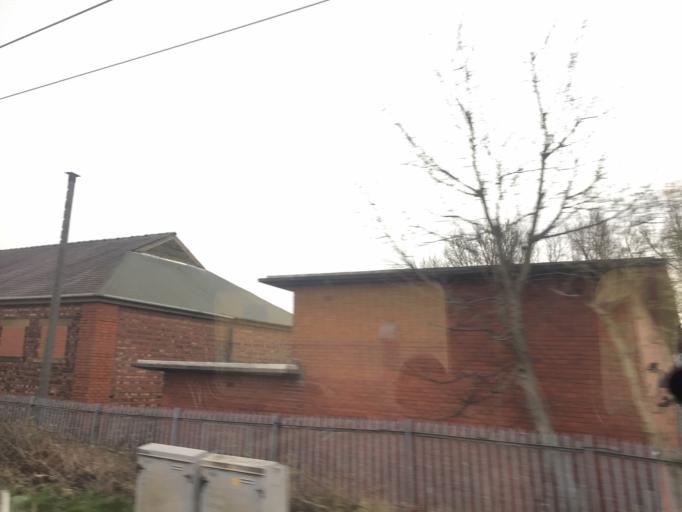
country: GB
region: England
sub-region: Borough of Wigan
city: Golborne
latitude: 53.4746
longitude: -2.5953
